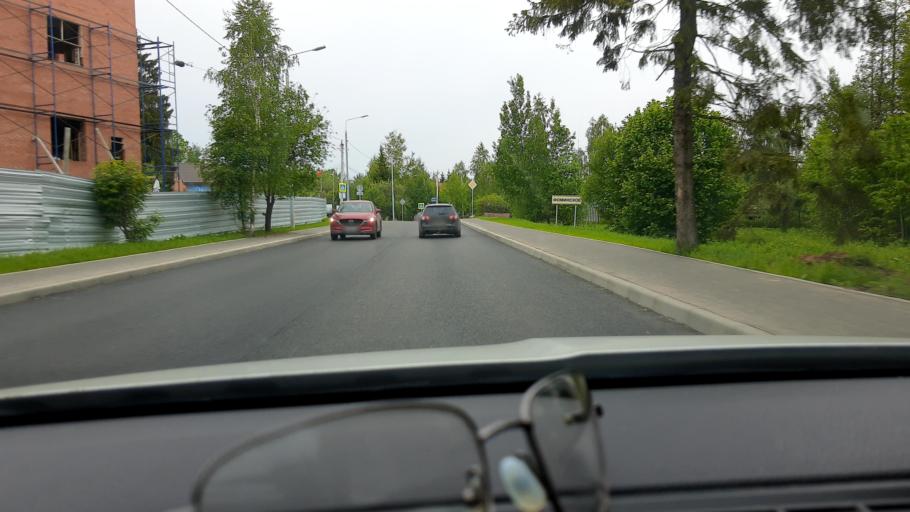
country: RU
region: Moskovskaya
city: Vatutinki
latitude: 55.5171
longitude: 37.3270
